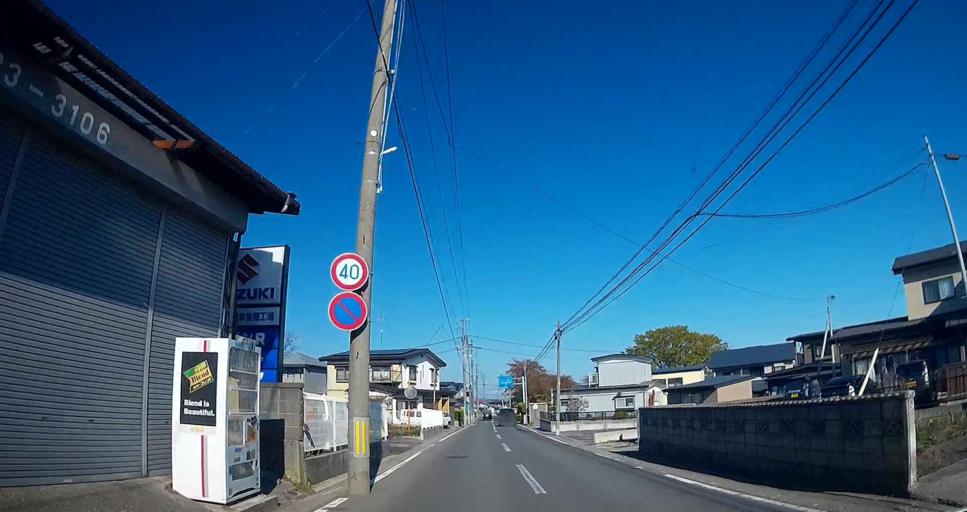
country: JP
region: Aomori
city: Hachinohe
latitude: 40.5243
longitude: 141.5532
